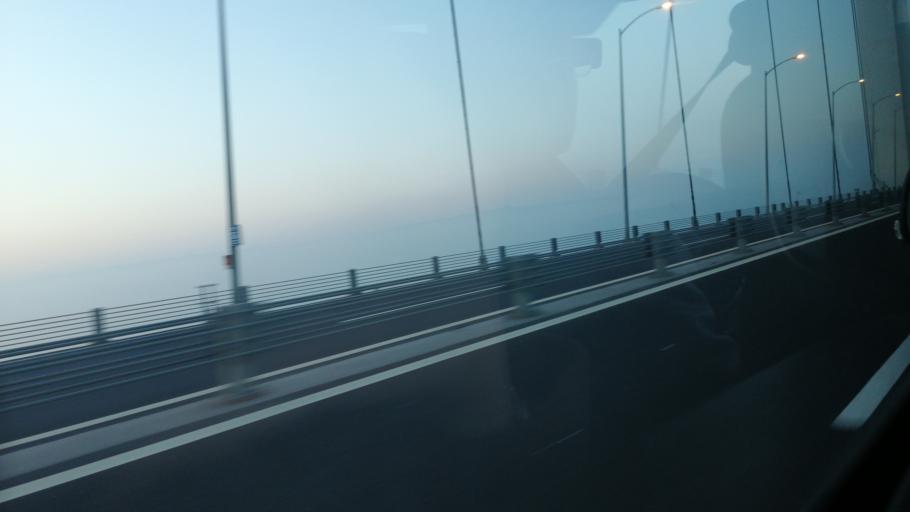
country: TR
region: Kocaeli
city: Tavsancil
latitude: 40.7604
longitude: 29.5168
